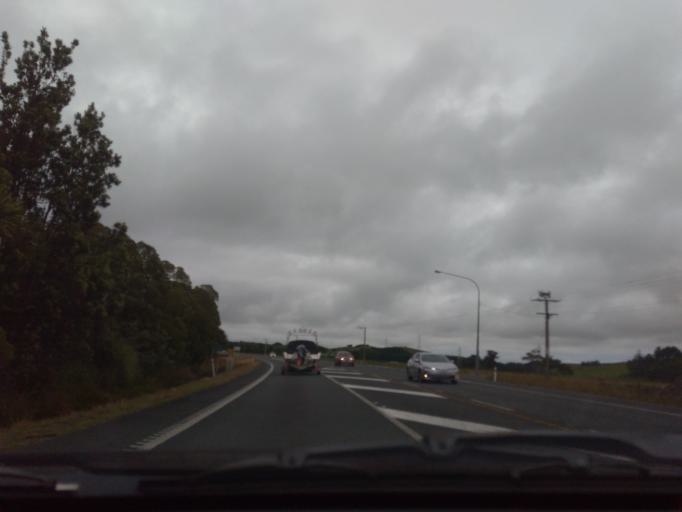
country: NZ
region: Northland
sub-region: Whangarei
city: Ruakaka
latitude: -36.0203
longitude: 174.4186
